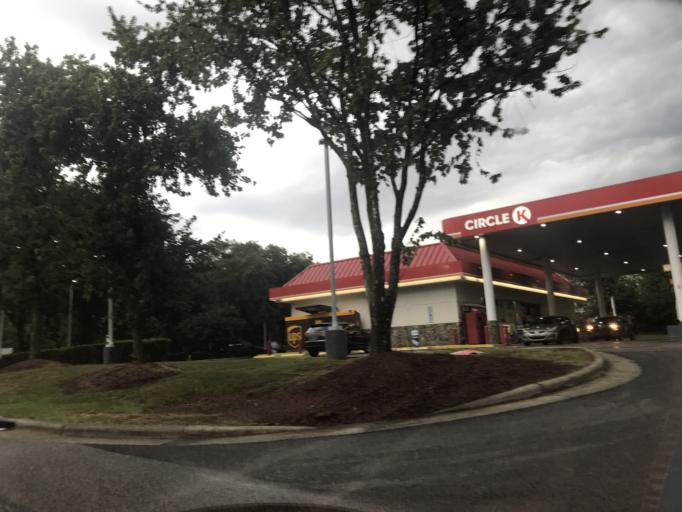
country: US
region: North Carolina
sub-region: Wake County
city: West Raleigh
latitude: 35.7478
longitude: -78.7020
